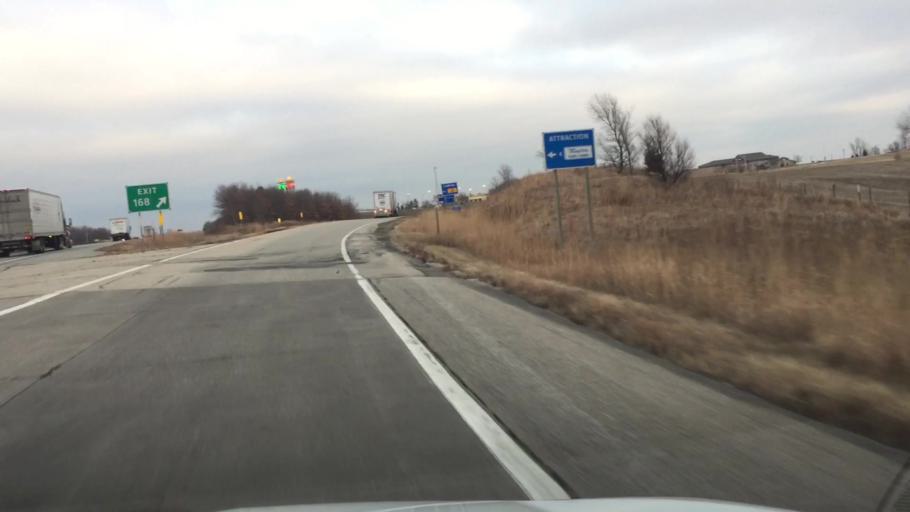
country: US
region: Iowa
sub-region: Jasper County
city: Newton
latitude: 41.6826
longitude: -93.0057
